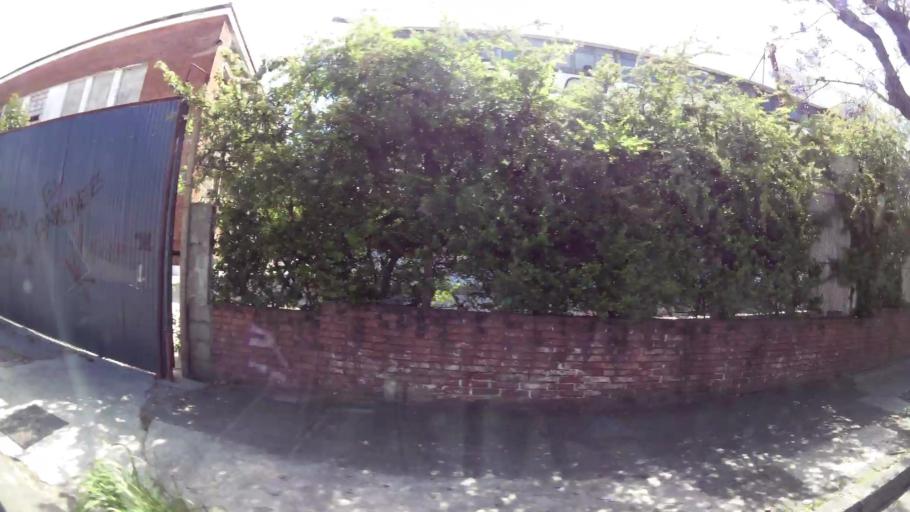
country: UY
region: Montevideo
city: Montevideo
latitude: -34.8598
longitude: -56.1426
